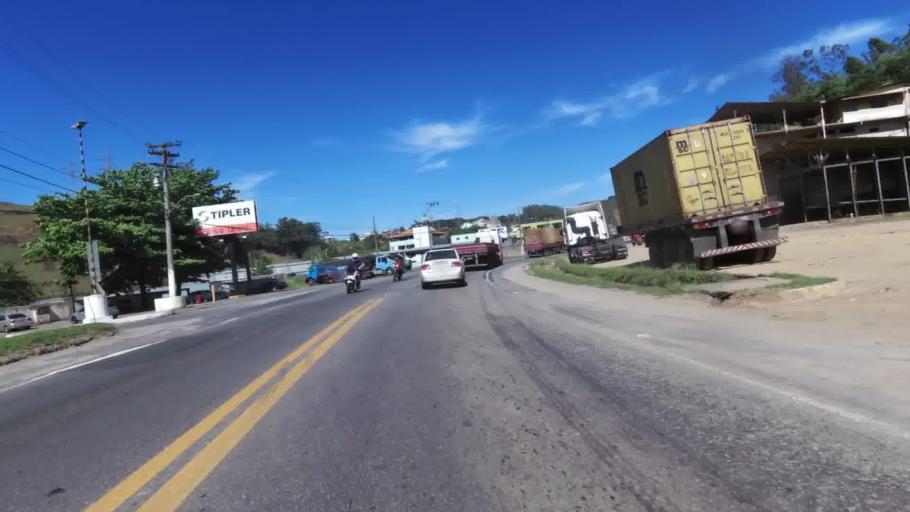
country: BR
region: Espirito Santo
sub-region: Iconha
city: Iconha
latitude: -20.7919
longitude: -40.8050
